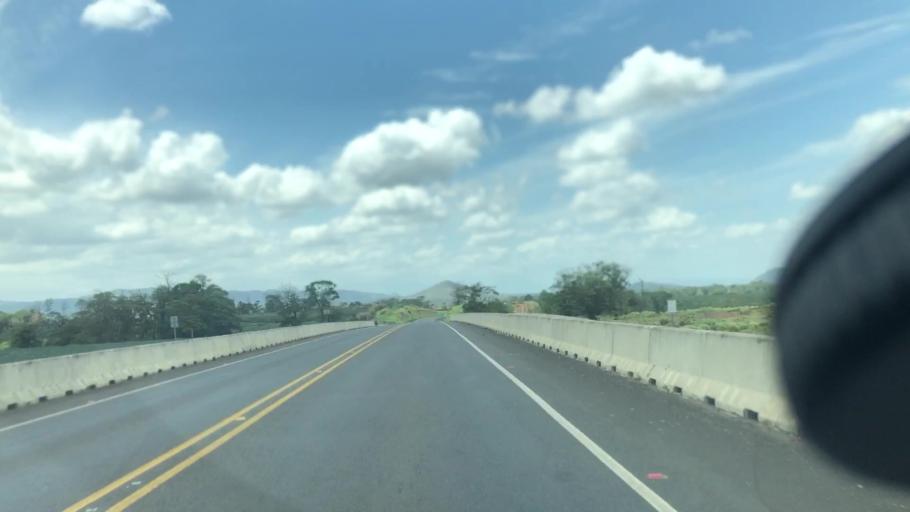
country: CR
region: Alajuela
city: Pital
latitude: 10.4345
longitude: -84.2776
